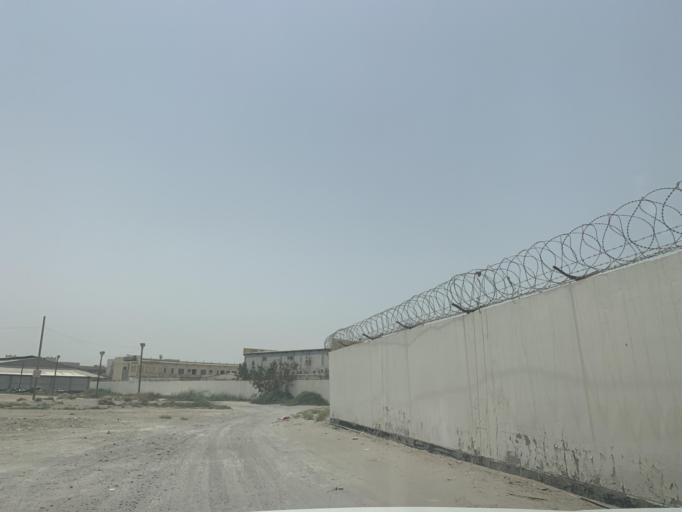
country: BH
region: Manama
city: Jidd Hafs
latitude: 26.2102
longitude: 50.5411
